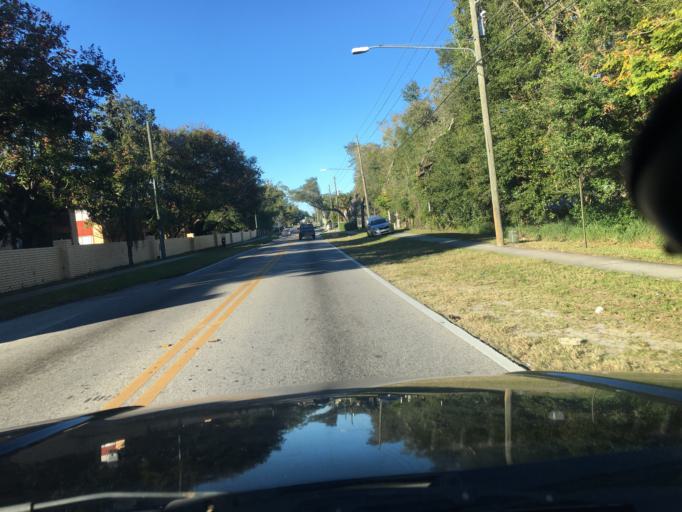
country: US
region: Florida
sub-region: Orange County
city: Pine Hills
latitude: 28.5798
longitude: -81.4678
